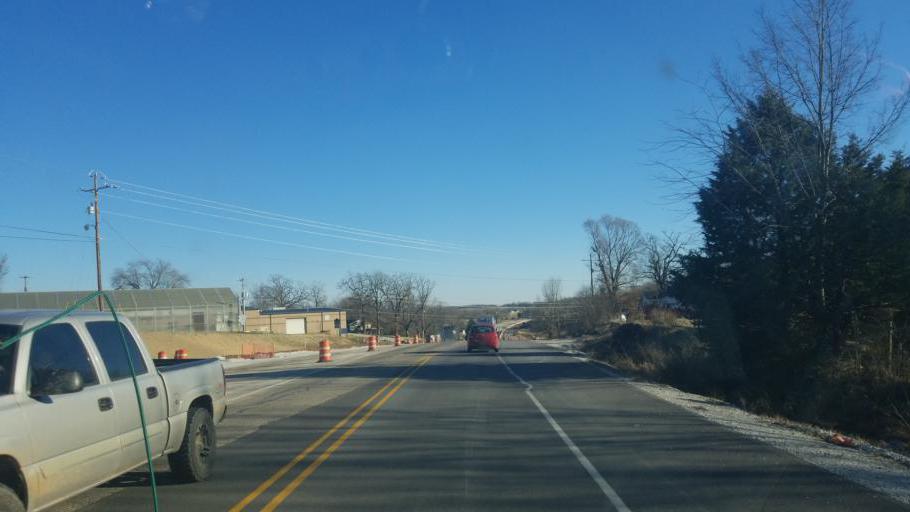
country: US
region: Arkansas
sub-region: Boone County
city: Harrison
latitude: 36.1583
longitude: -92.9961
